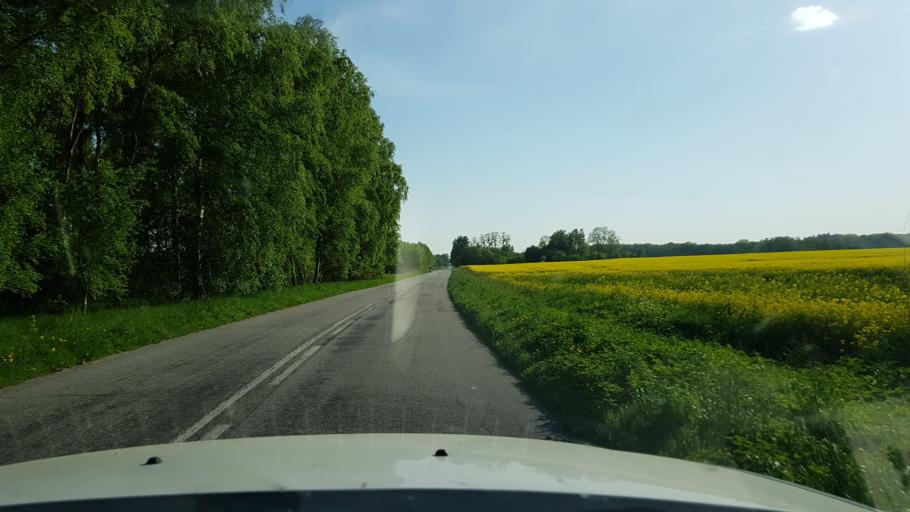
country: PL
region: West Pomeranian Voivodeship
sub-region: Powiat lobeski
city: Resko
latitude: 53.7495
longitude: 15.3730
